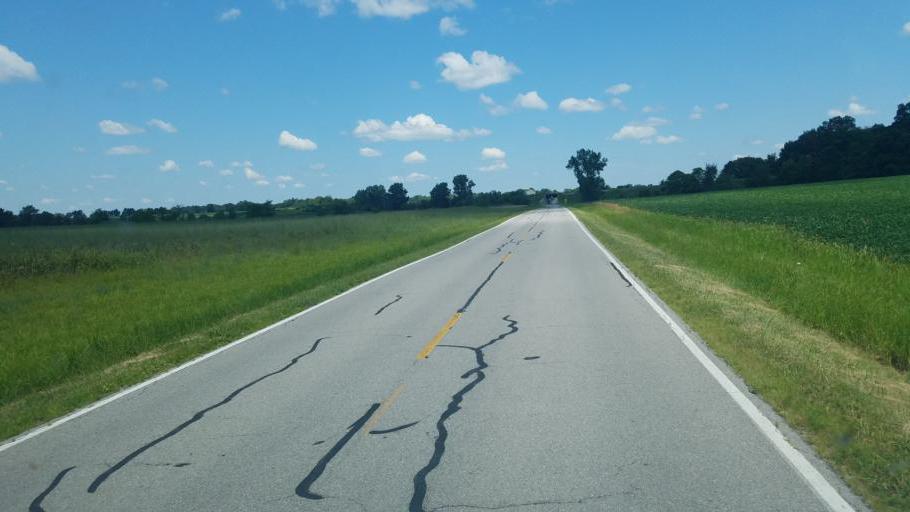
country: US
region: Ohio
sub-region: Marion County
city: Marion
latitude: 40.6296
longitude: -83.1733
